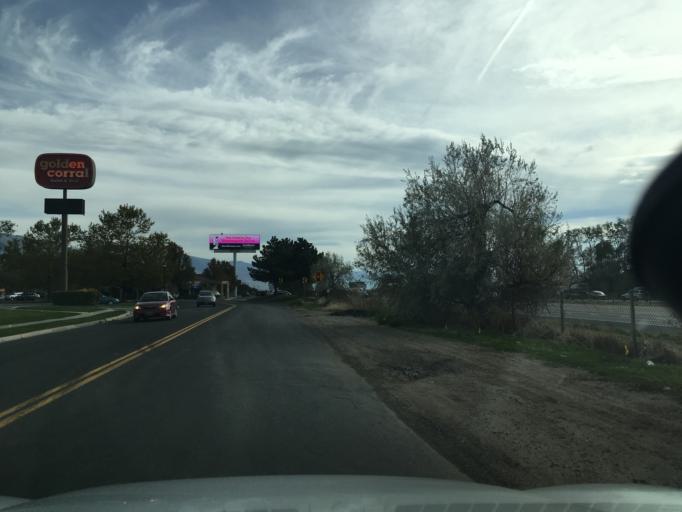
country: US
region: Utah
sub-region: Davis County
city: Hill Air Force Bace
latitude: 41.0845
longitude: -111.9859
